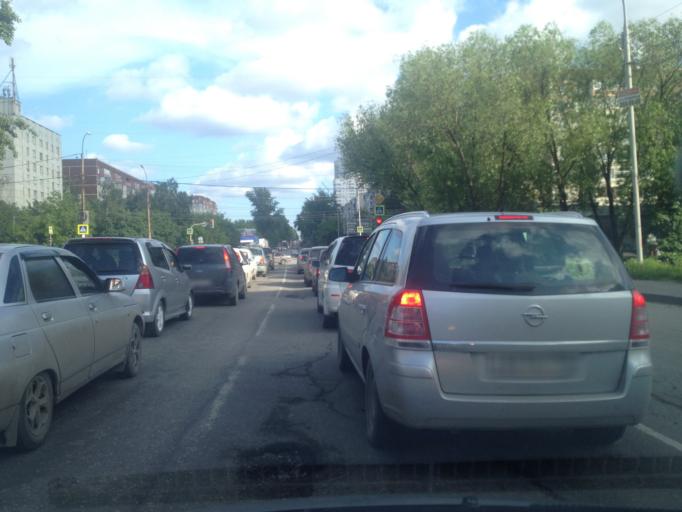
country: RU
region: Sverdlovsk
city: Yekaterinburg
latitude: 56.9032
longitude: 60.6240
